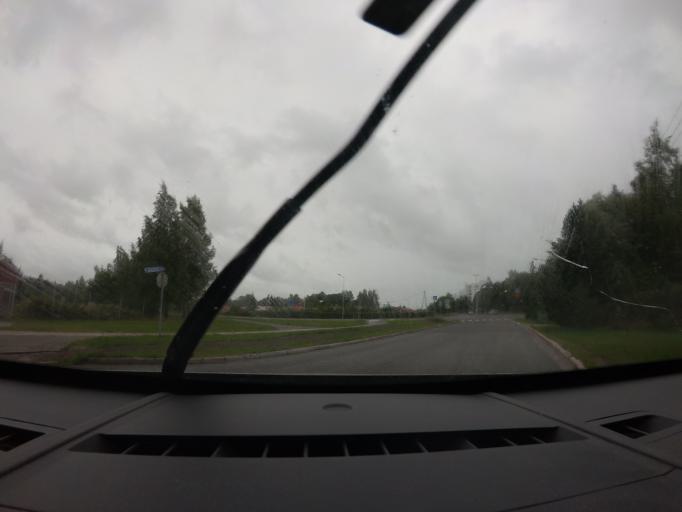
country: FI
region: Varsinais-Suomi
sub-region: Turku
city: Turku
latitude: 60.4240
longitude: 22.2952
